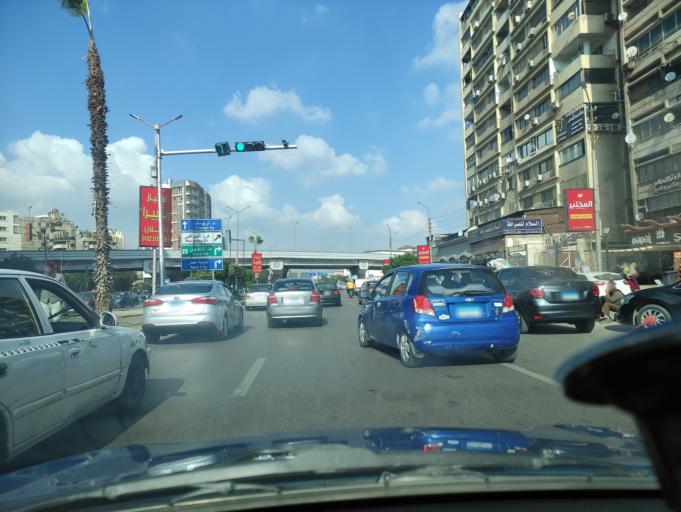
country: EG
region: Muhafazat al Qahirah
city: Cairo
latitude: 30.0896
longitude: 31.3415
